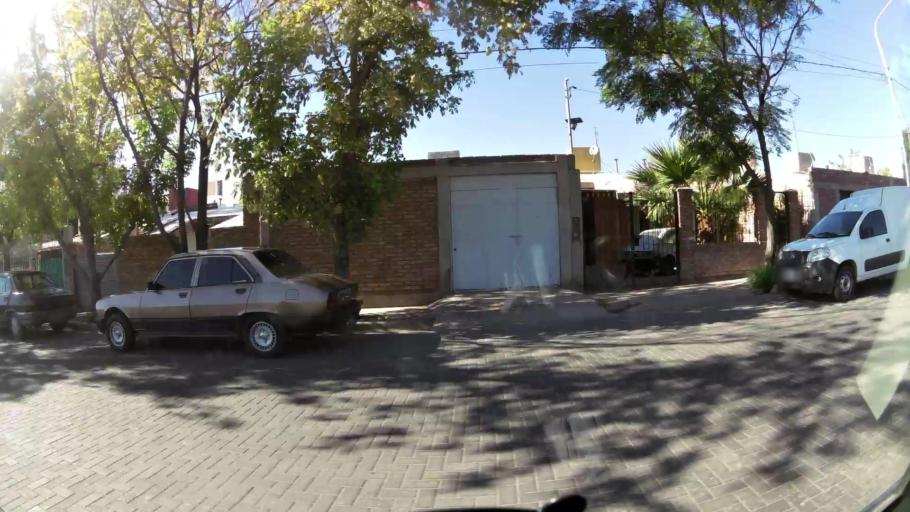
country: AR
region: Mendoza
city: Las Heras
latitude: -32.8712
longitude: -68.8643
